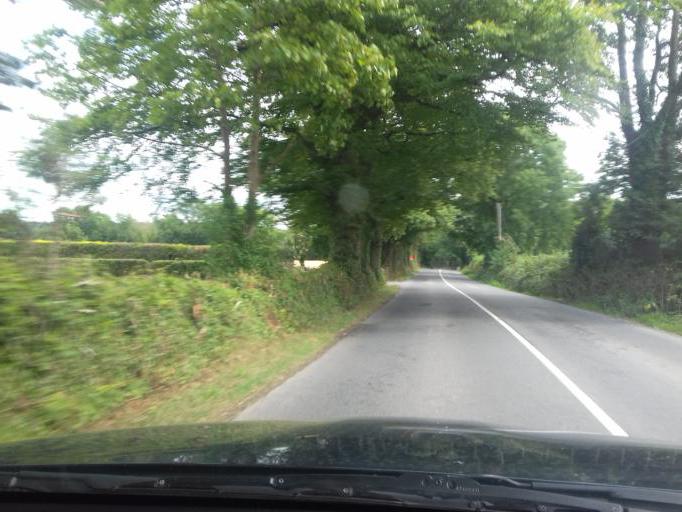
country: IE
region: Leinster
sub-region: Loch Garman
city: Enniscorthy
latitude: 52.4891
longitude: -6.4982
